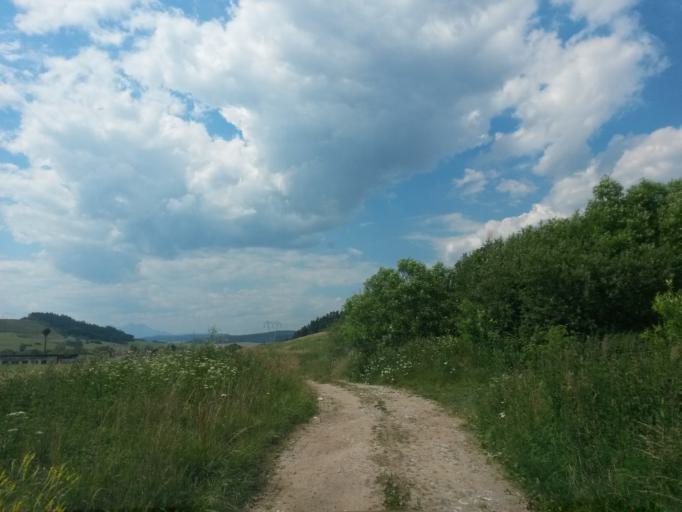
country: SK
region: Kosicky
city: Spisska Nova Ves
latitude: 48.9473
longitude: 20.5983
